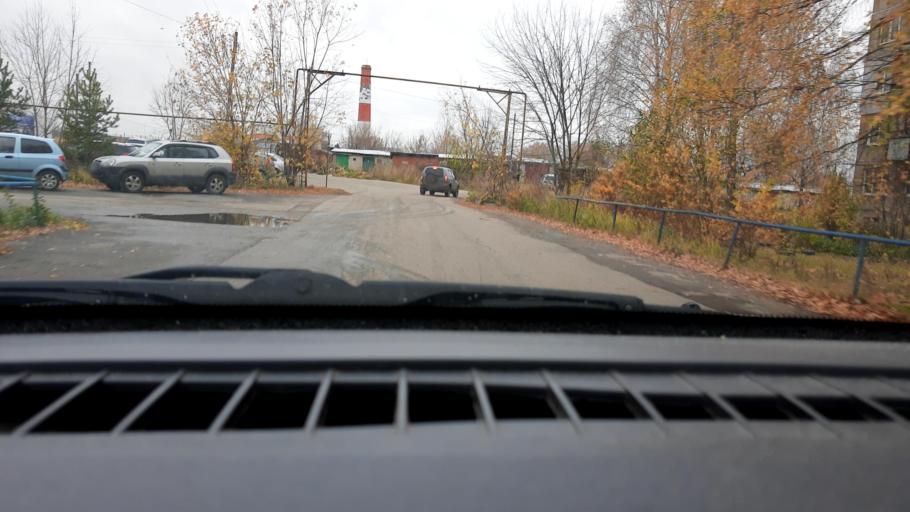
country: RU
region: Nizjnij Novgorod
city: Afonino
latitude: 56.2127
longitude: 44.0994
